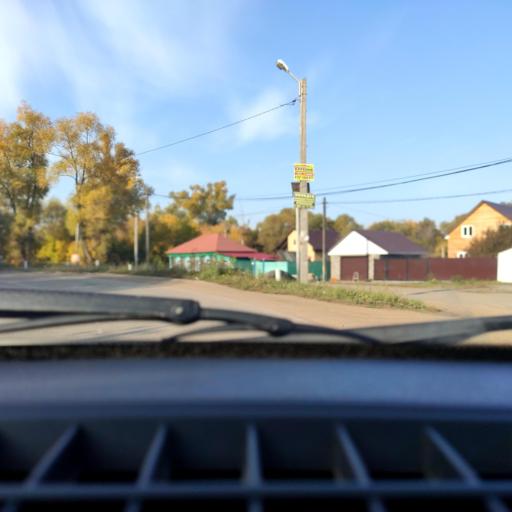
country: RU
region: Bashkortostan
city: Avdon
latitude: 54.6555
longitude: 55.7648
